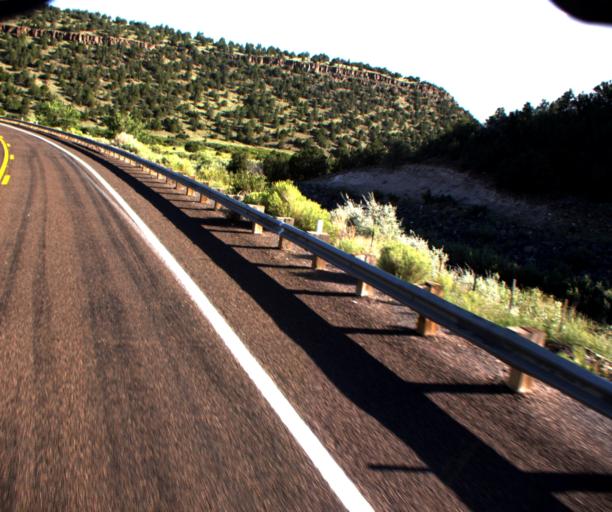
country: US
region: Arizona
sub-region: Apache County
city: Eagar
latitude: 34.0903
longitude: -109.2025
